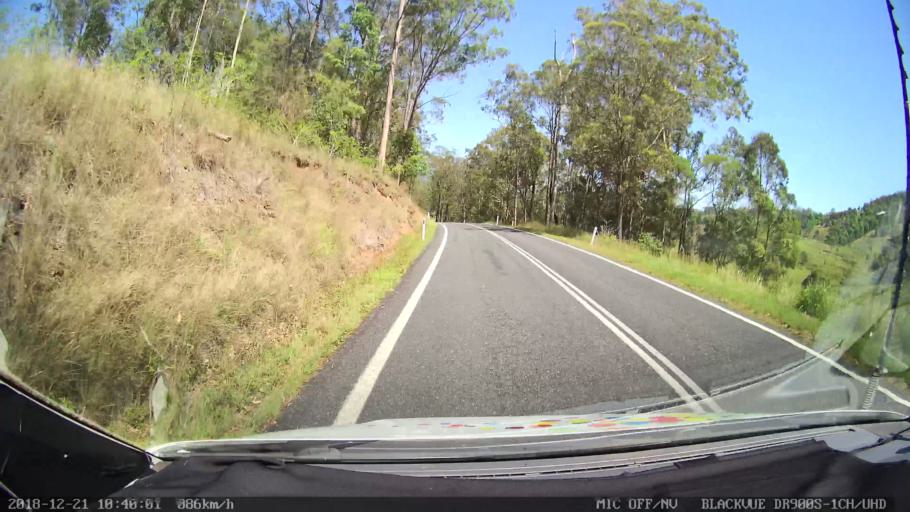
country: AU
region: New South Wales
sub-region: Clarence Valley
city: Gordon
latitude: -29.6033
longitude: 152.5901
